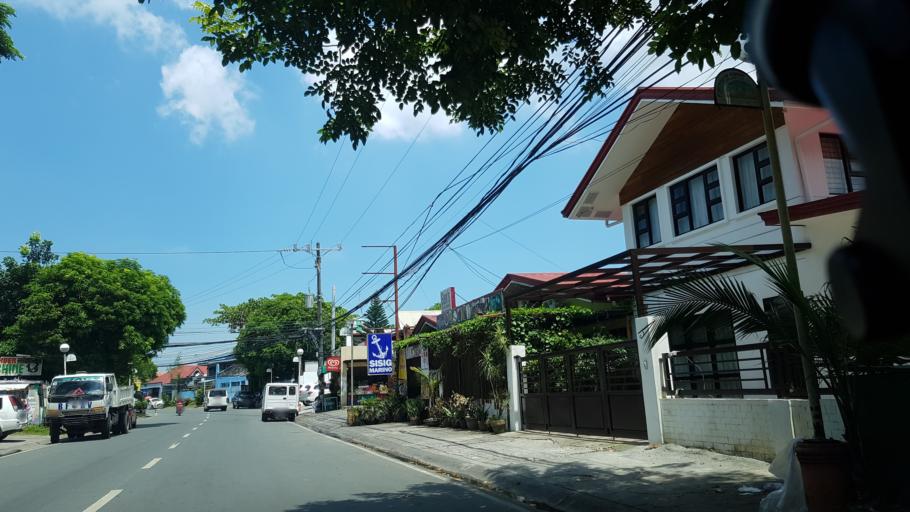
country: PH
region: Calabarzon
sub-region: Province of Rizal
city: Las Pinas
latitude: 14.4393
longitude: 120.9847
